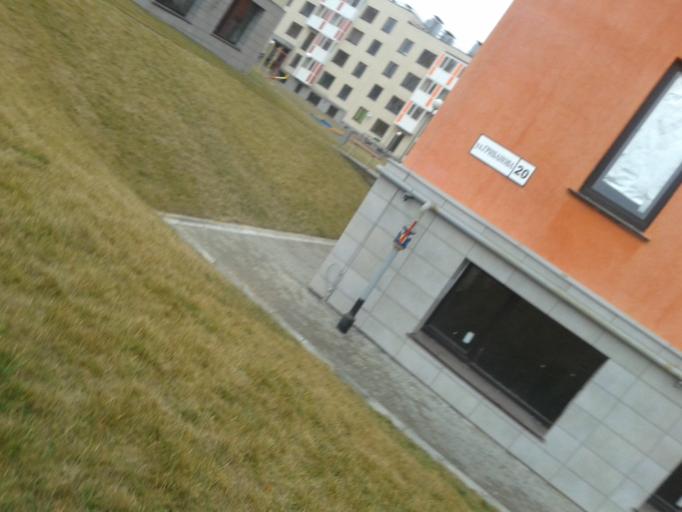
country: RU
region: Volgograd
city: Volgograd
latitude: 48.6635
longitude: 44.4110
